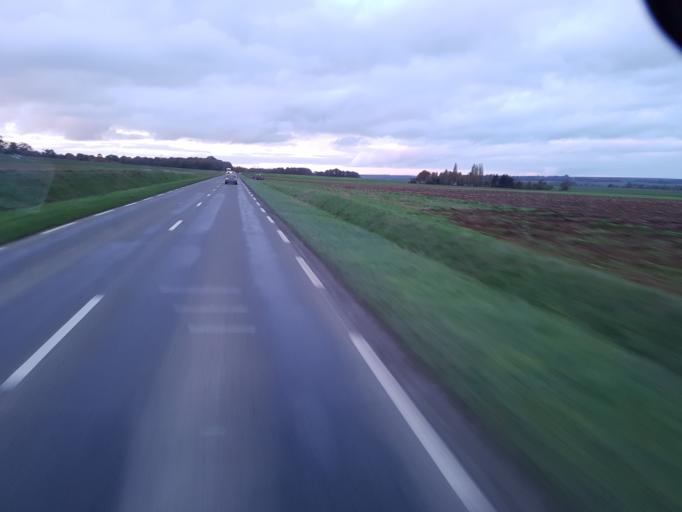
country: FR
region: Picardie
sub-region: Departement de l'Aisne
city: Coincy
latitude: 49.1630
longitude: 3.3803
